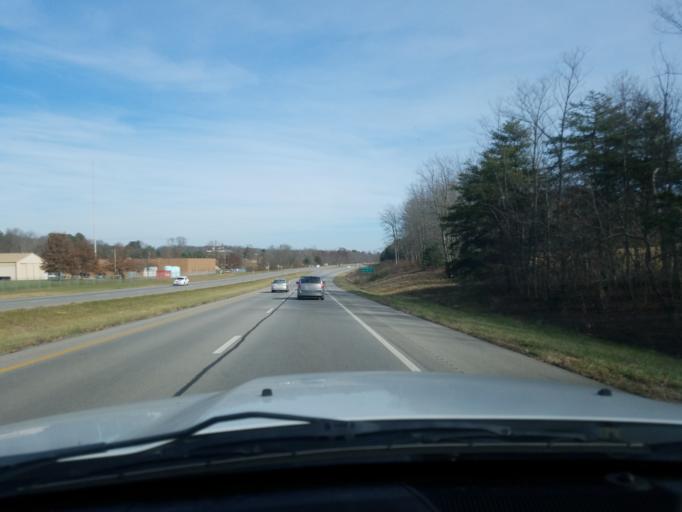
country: US
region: Ohio
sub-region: Jackson County
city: Jackson
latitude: 39.0687
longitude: -82.5759
